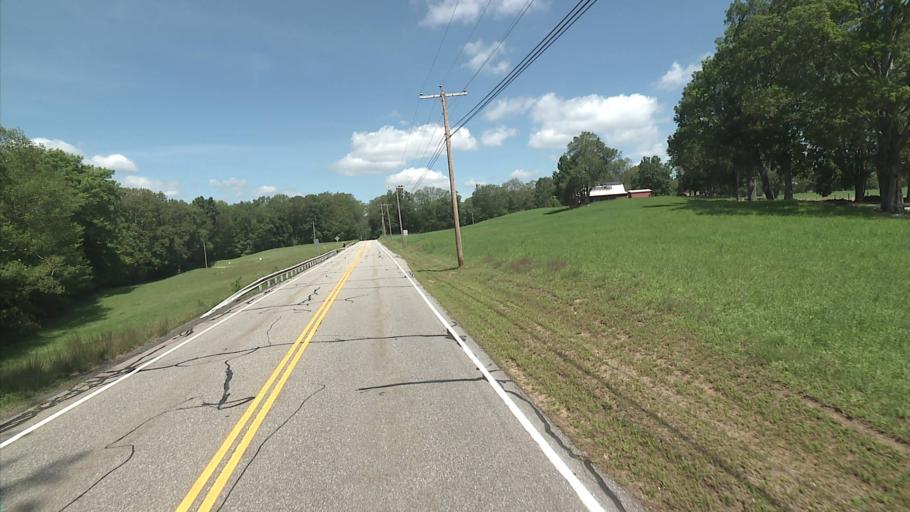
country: US
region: Connecticut
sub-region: Windham County
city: South Woodstock
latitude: 41.9195
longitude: -72.0790
